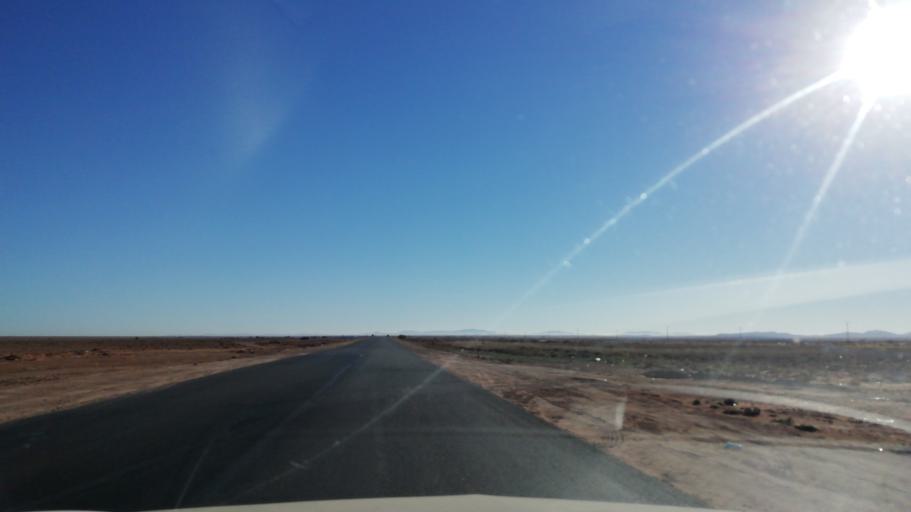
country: DZ
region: El Bayadh
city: El Bayadh
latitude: 33.8577
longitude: 0.5784
